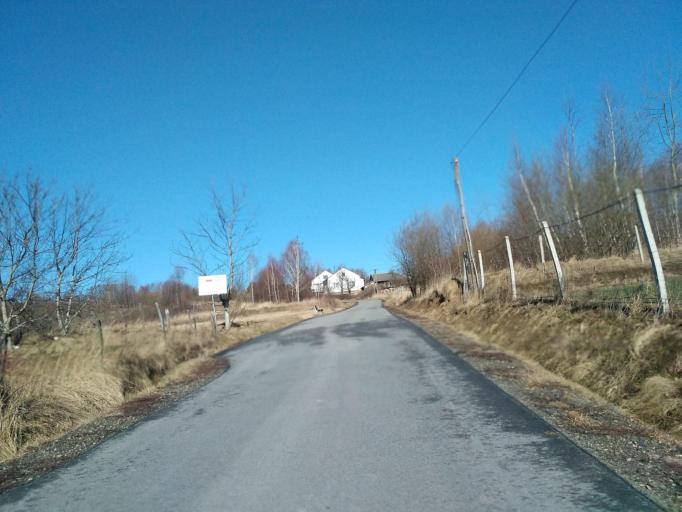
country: PL
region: Subcarpathian Voivodeship
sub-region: Powiat rzeszowski
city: Lubenia
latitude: 49.9285
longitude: 21.9489
